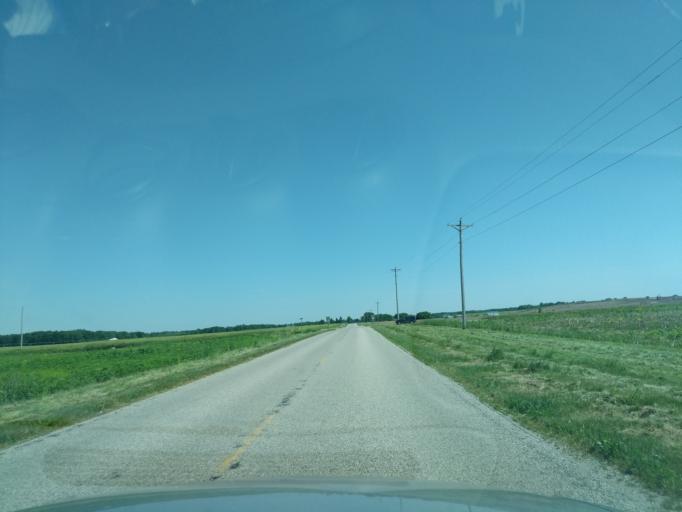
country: US
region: Indiana
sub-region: Huntington County
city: Huntington
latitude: 40.8133
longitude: -85.5081
